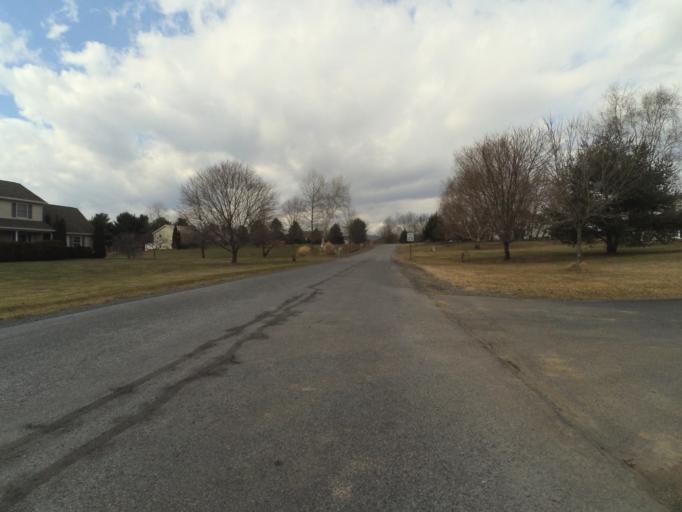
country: US
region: Pennsylvania
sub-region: Centre County
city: Stormstown
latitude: 40.7649
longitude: -78.0377
